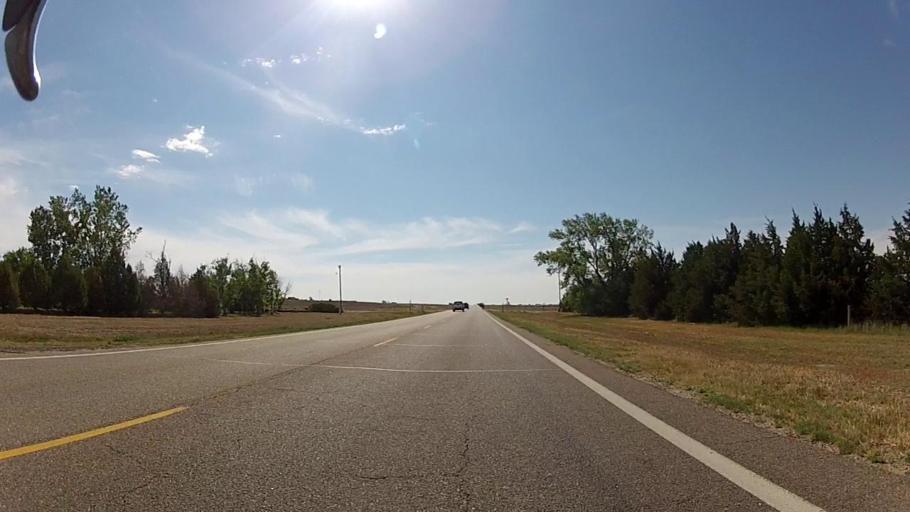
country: US
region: Kansas
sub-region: Grant County
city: Ulysses
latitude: 37.5699
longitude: -101.3284
